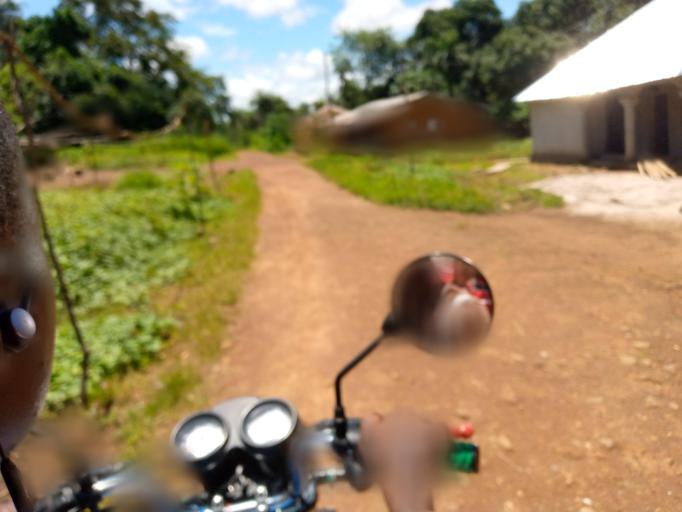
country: SL
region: Northern Province
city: Binkolo
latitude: 9.0996
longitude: -12.1430
